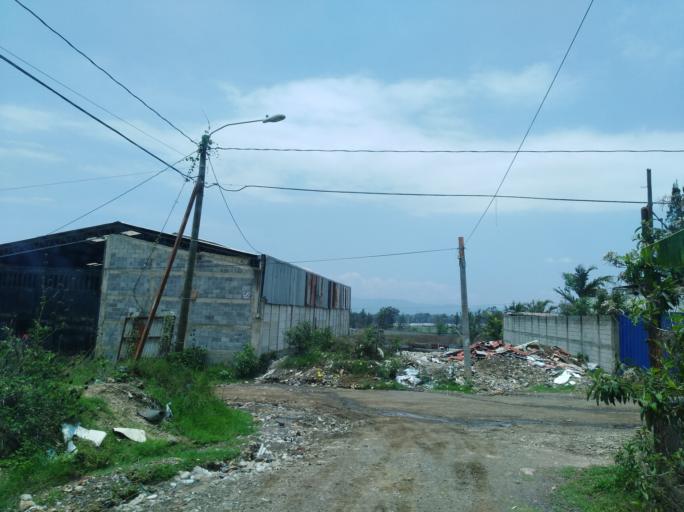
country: GT
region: Guatemala
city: Villa Nueva
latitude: 14.5271
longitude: -90.6198
